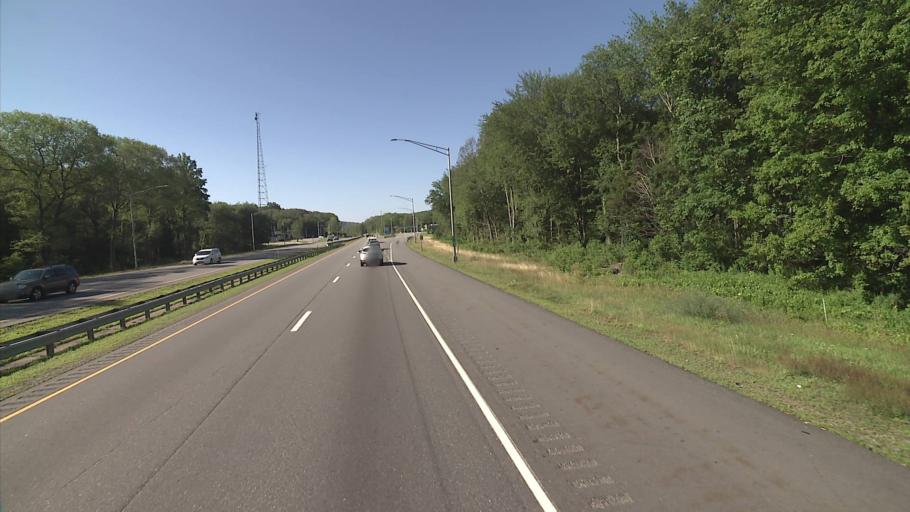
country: US
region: Connecticut
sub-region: New London County
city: Oxoboxo River
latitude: 41.4766
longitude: -72.1165
